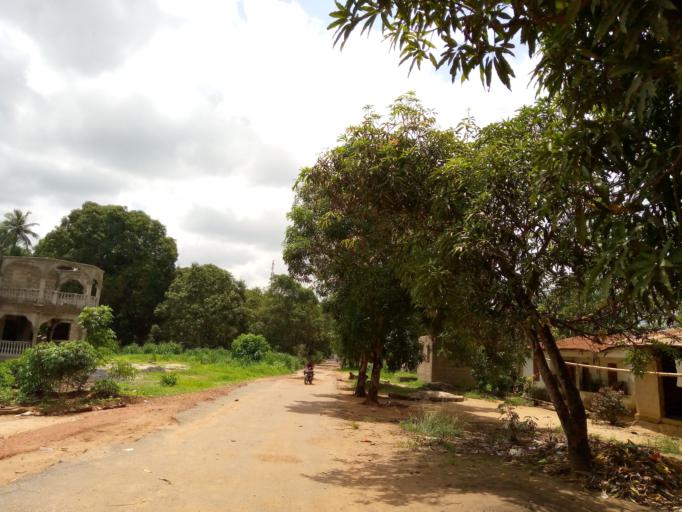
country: SL
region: Western Area
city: Waterloo
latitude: 8.3900
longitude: -12.9482
